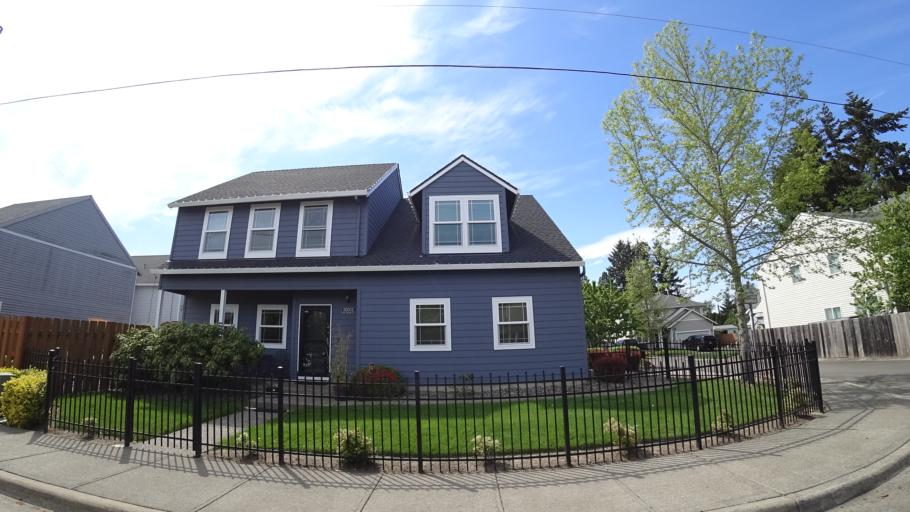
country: US
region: Oregon
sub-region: Washington County
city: Aloha
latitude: 45.4881
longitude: -122.8831
